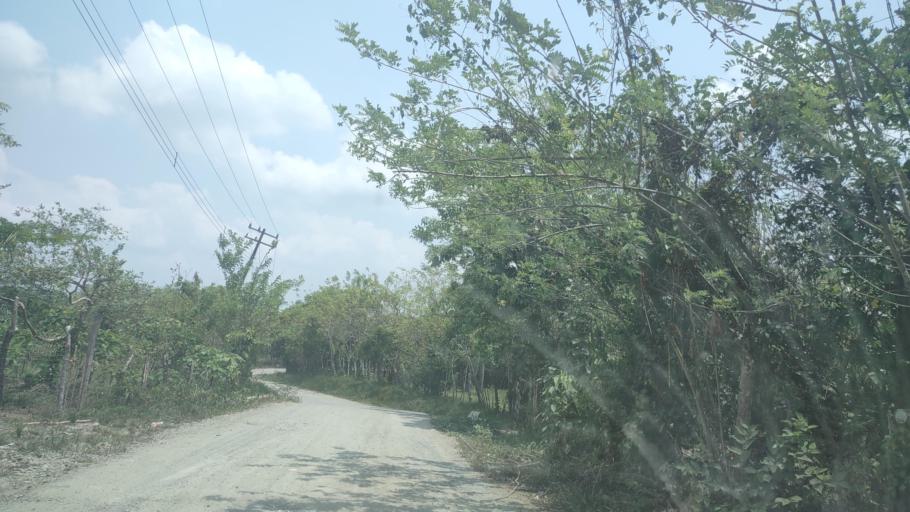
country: MX
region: Tabasco
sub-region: Huimanguillo
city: Francisco Rueda
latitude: 17.5846
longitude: -93.9592
